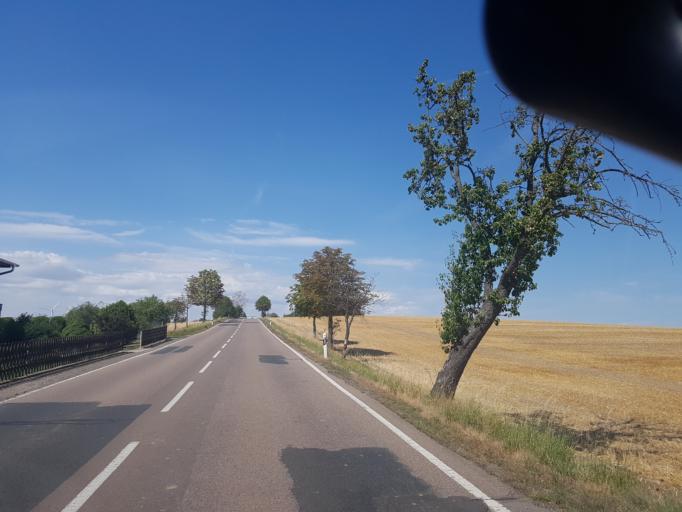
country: DE
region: Saxony
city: Hartha
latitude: 51.0852
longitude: 12.9872
